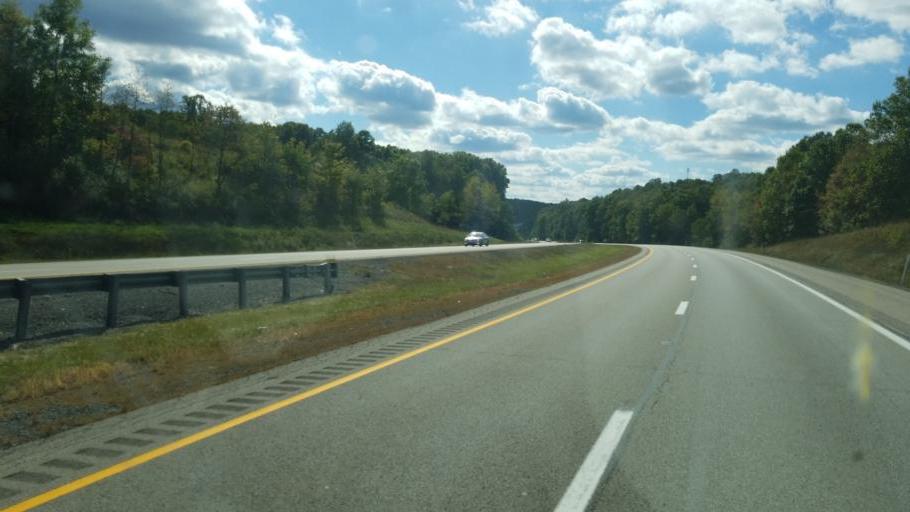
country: US
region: West Virginia
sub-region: Monongalia County
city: Cheat Lake
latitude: 39.6629
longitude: -79.6744
